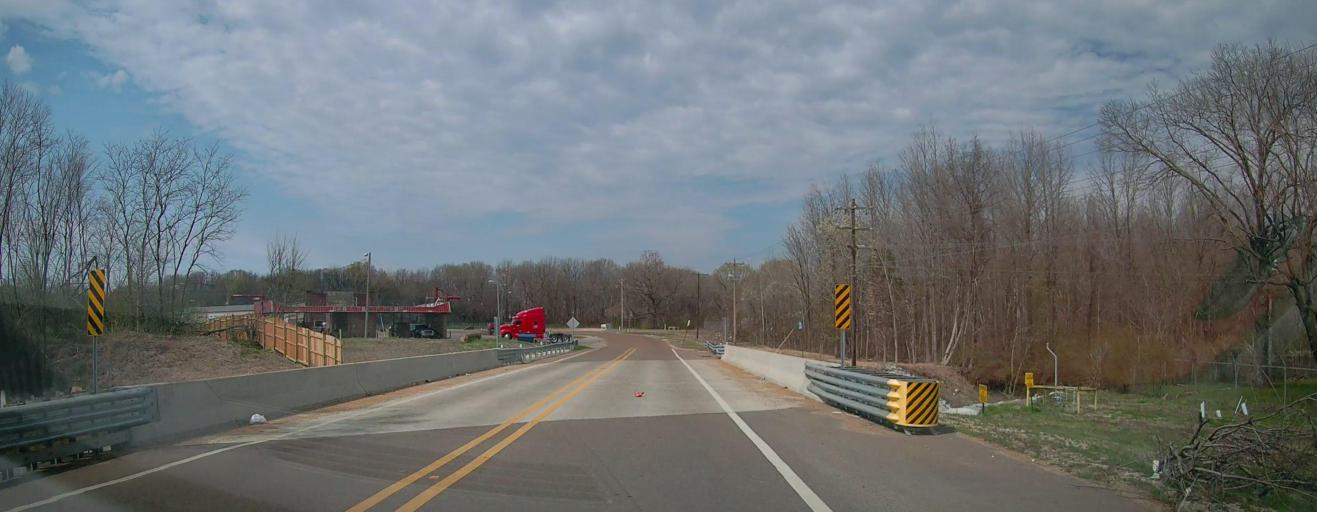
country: US
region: Mississippi
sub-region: De Soto County
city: Olive Branch
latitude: 34.9913
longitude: -89.8651
